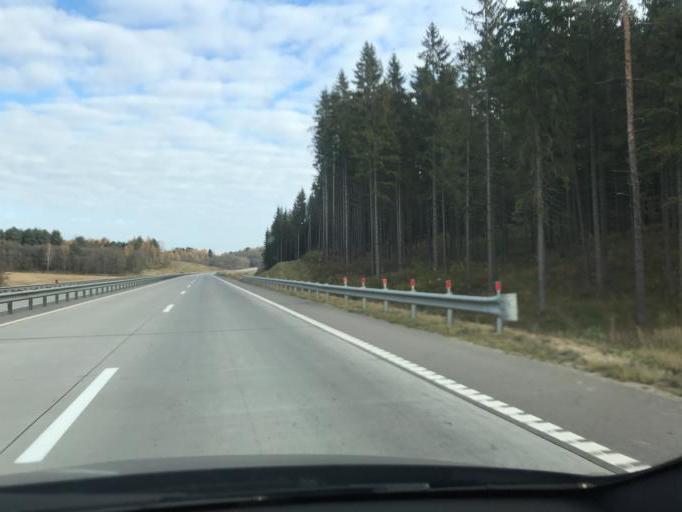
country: BY
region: Minsk
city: Pyatryshki
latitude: 54.0446
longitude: 27.1796
